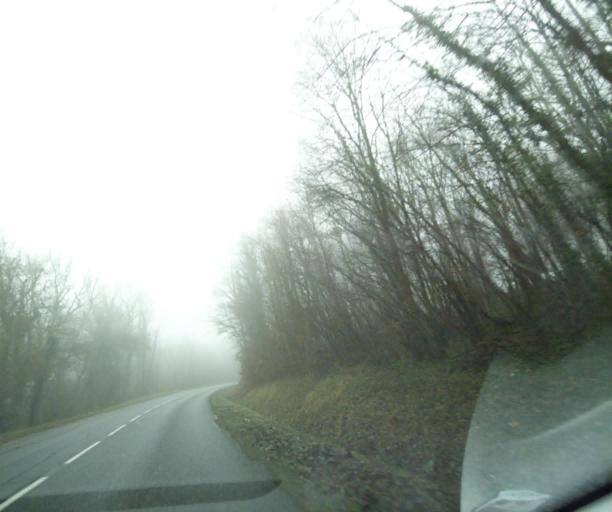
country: FR
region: Ile-de-France
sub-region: Departement de Seine-et-Marne
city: Saint-Mard
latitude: 49.0456
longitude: 2.6882
